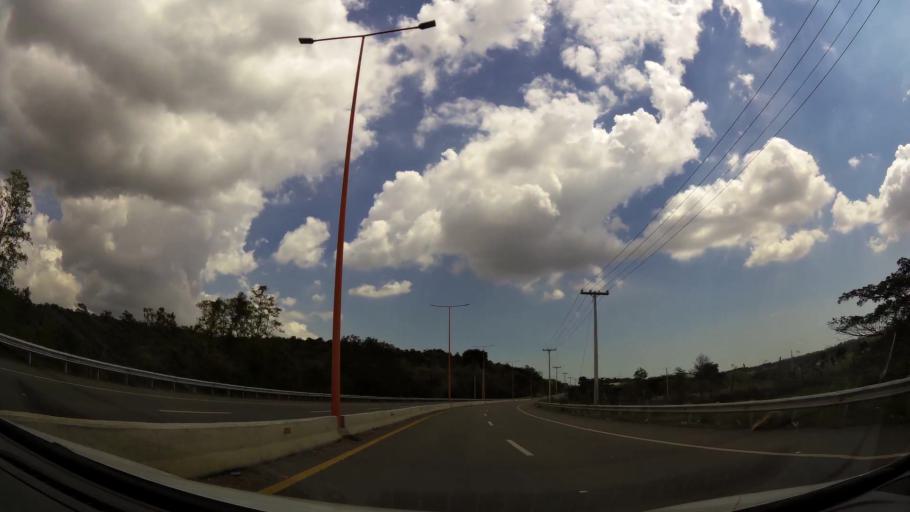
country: DO
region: Nacional
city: Santo Domingo
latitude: 18.5547
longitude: -69.9728
